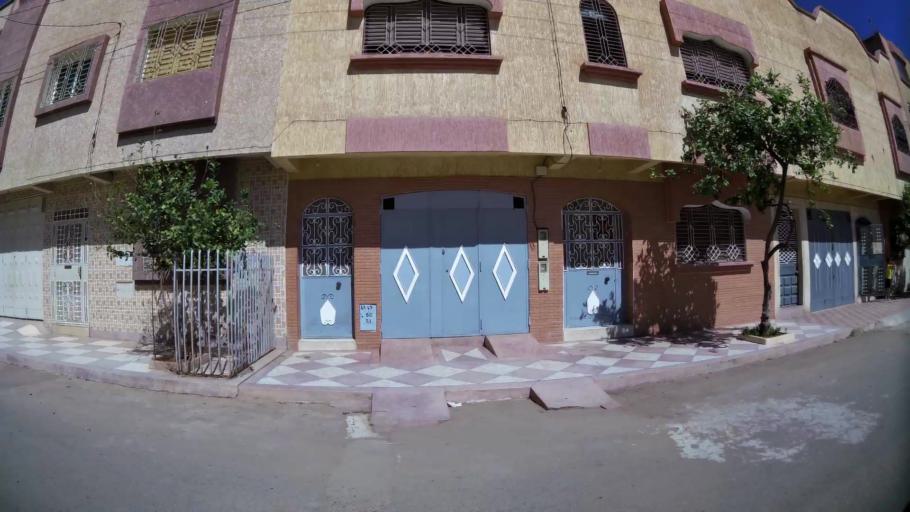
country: MA
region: Oriental
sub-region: Oujda-Angad
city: Oujda
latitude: 34.6627
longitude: -1.9287
